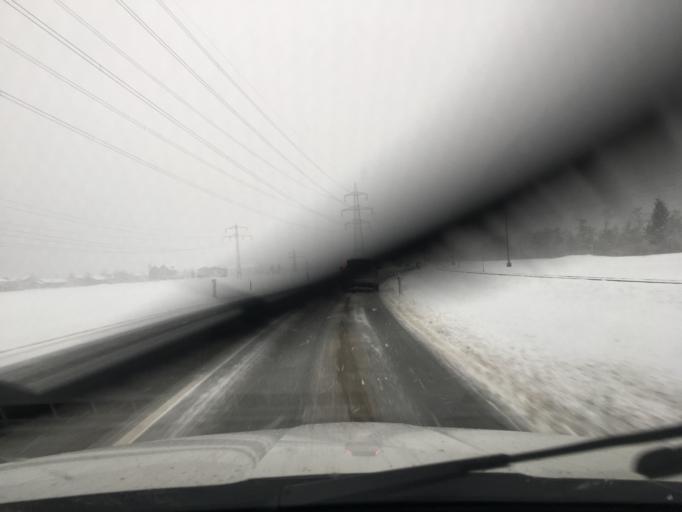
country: AT
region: Tyrol
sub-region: Politischer Bezirk Schwaz
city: Mayrhofen
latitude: 47.1814
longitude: 11.8666
